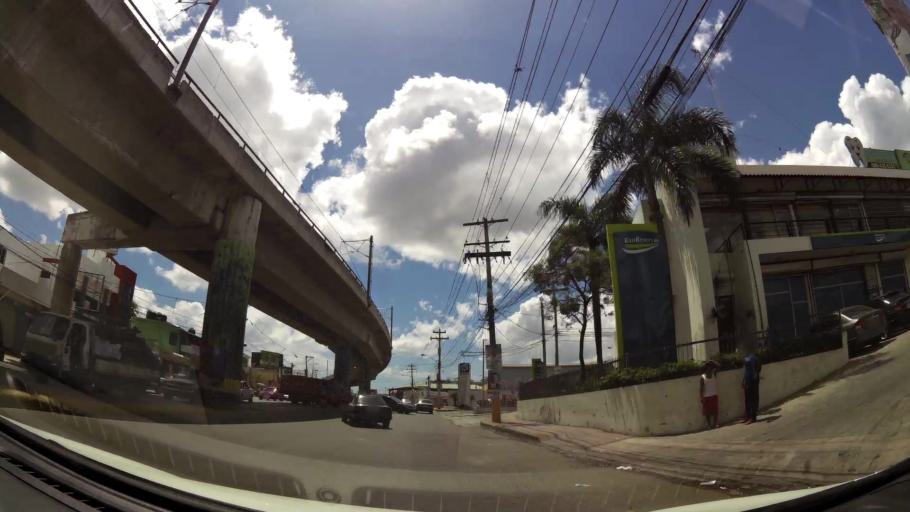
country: DO
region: Nacional
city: La Agustina
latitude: 18.5228
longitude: -69.9174
